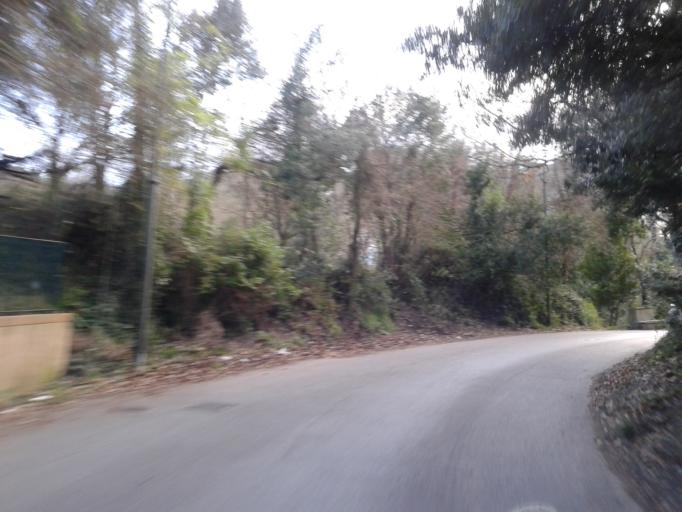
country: IT
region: Tuscany
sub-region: Provincia di Livorno
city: Quercianella
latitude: 43.4957
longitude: 10.3562
